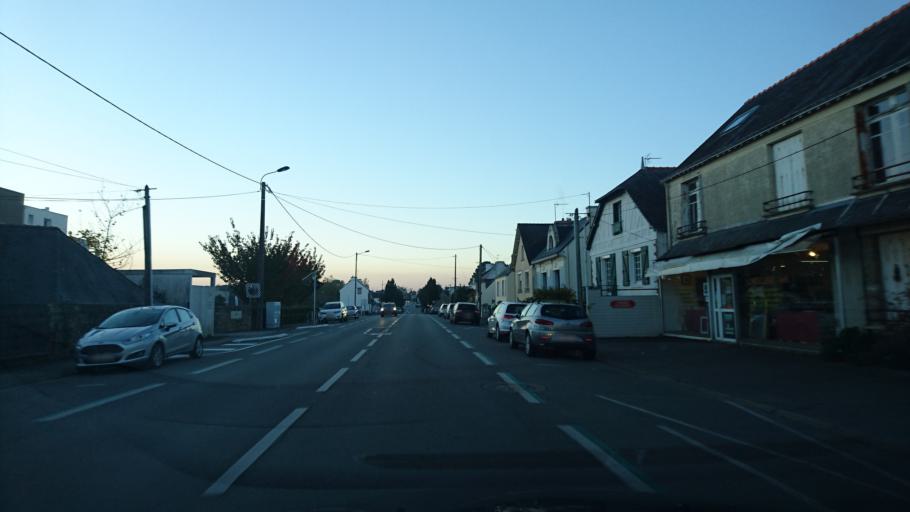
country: FR
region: Brittany
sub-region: Departement du Morbihan
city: Auray
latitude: 47.6761
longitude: -3.0049
